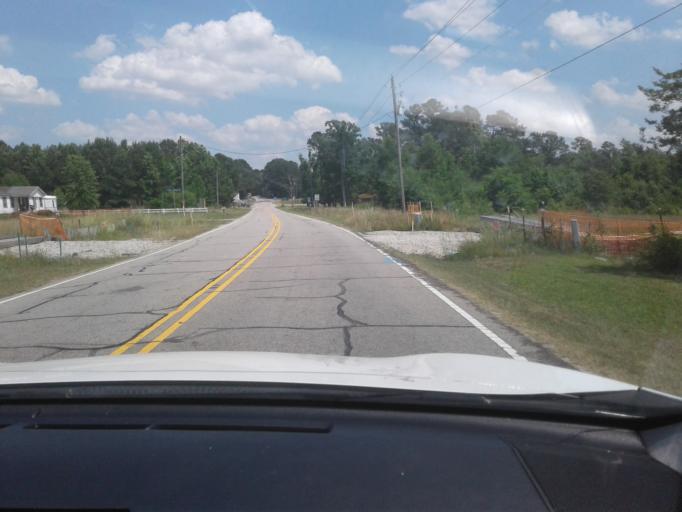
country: US
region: North Carolina
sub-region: Harnett County
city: Dunn
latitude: 35.2055
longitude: -78.6736
